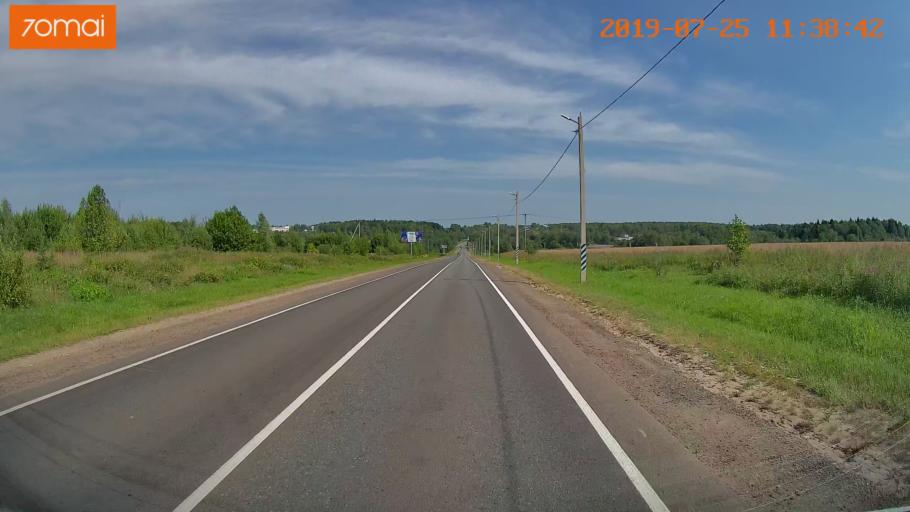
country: RU
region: Ivanovo
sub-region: Privolzhskiy Rayon
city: Ples
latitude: 57.4434
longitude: 41.4869
